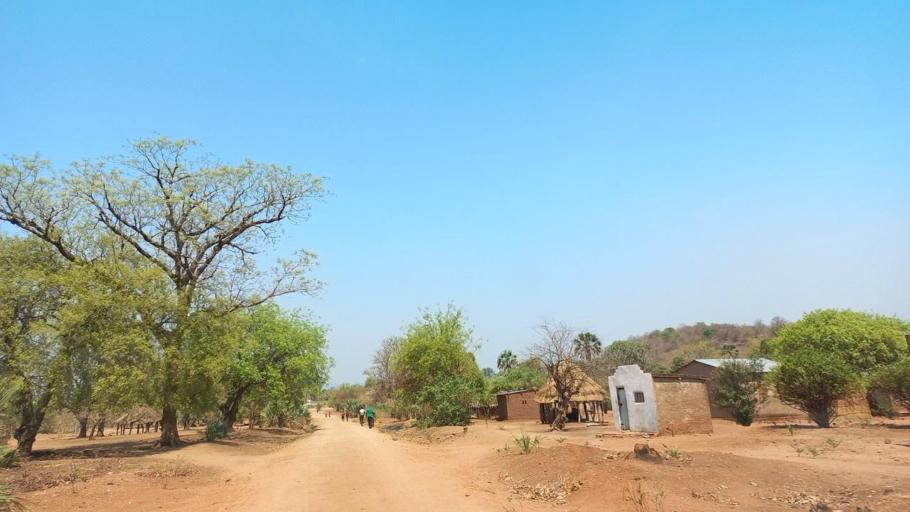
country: ZM
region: Lusaka
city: Luangwa
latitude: -15.1868
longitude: 30.2190
